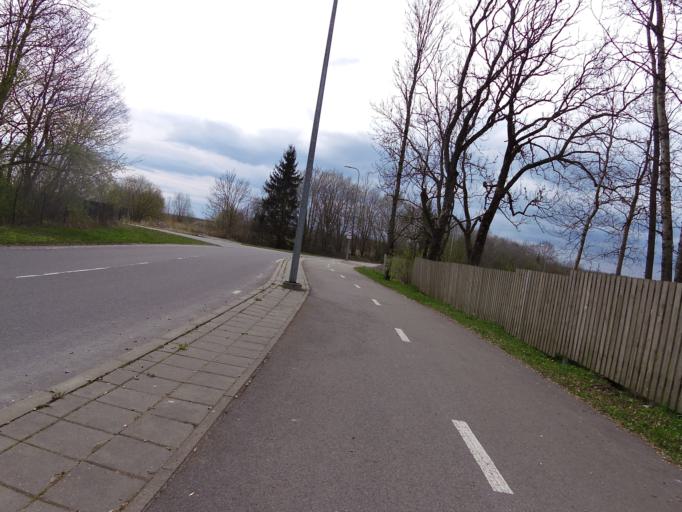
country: EE
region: Harju
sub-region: Kiili vald
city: Kiili
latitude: 59.3690
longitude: 24.8313
